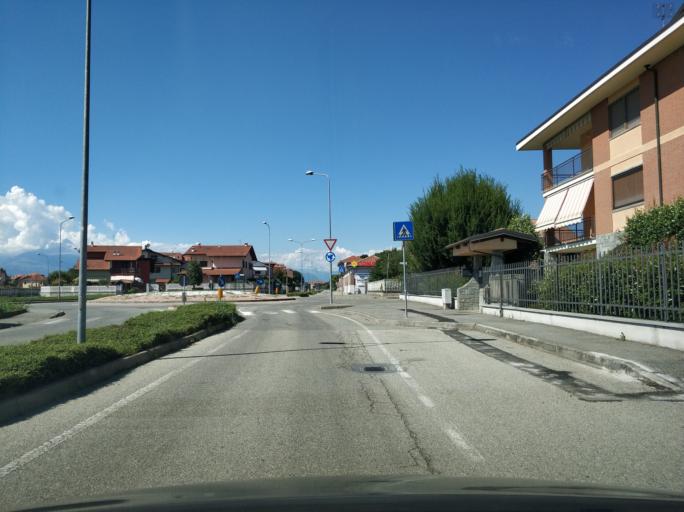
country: IT
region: Piedmont
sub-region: Provincia di Torino
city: San Benigno Canavese
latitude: 45.2261
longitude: 7.7784
